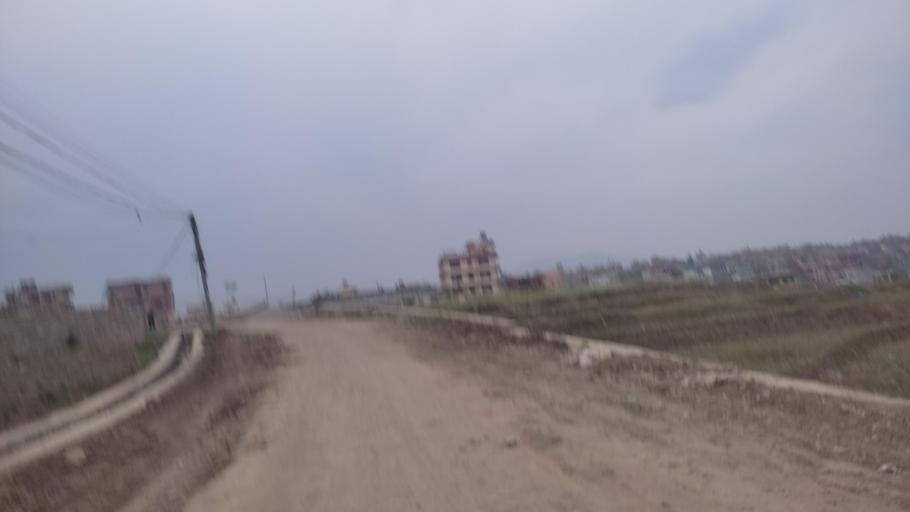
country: NP
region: Central Region
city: Kirtipur
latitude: 27.6630
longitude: 85.2775
